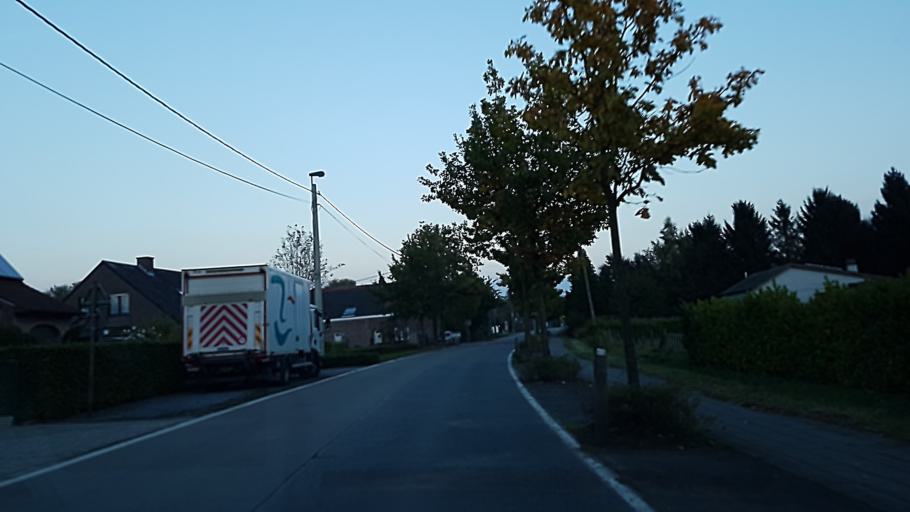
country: BE
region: Flanders
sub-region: Provincie Antwerpen
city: Rumst
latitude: 51.0799
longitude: 4.4631
